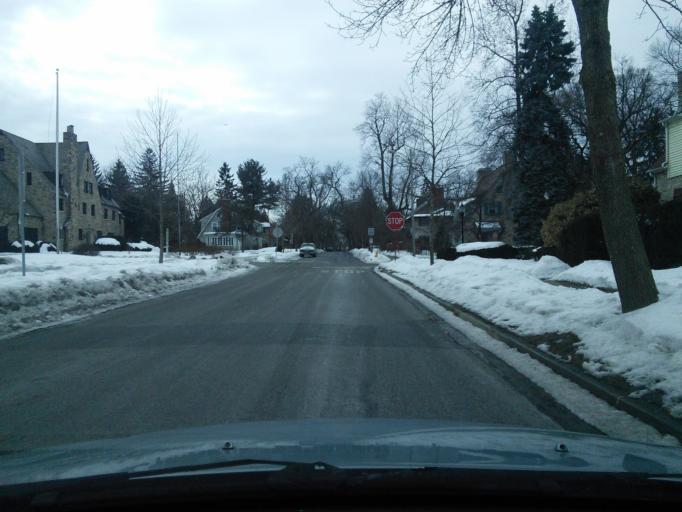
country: US
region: Pennsylvania
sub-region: Centre County
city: State College
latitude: 40.7955
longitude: -77.8514
